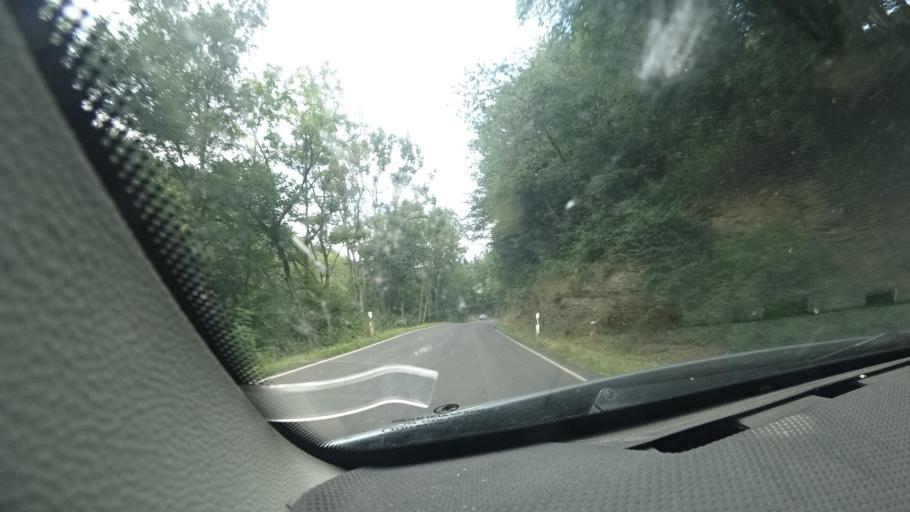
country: DE
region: Rheinland-Pfalz
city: Spessart
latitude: 50.4626
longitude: 7.0850
